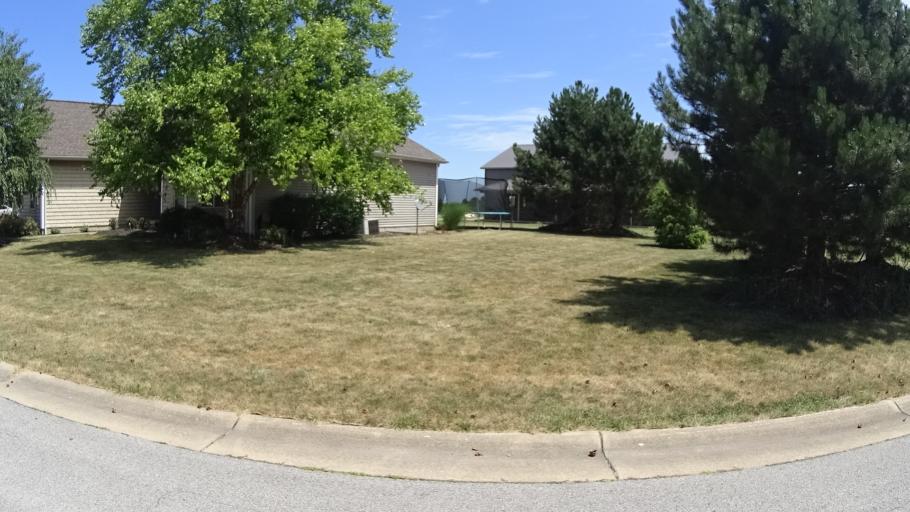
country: US
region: Ohio
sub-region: Erie County
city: Sandusky
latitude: 41.3863
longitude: -82.6633
